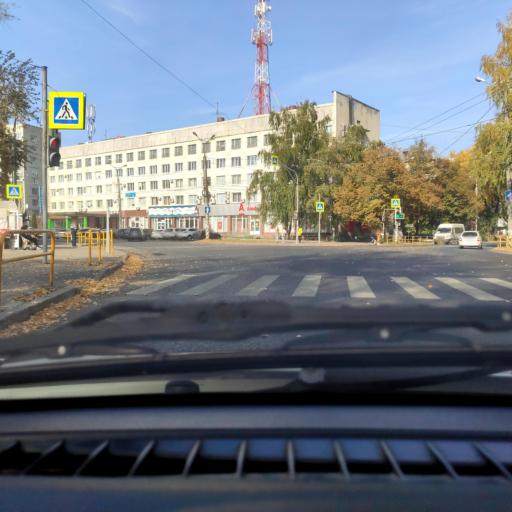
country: RU
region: Samara
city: Tol'yatti
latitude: 53.5109
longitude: 49.4219
